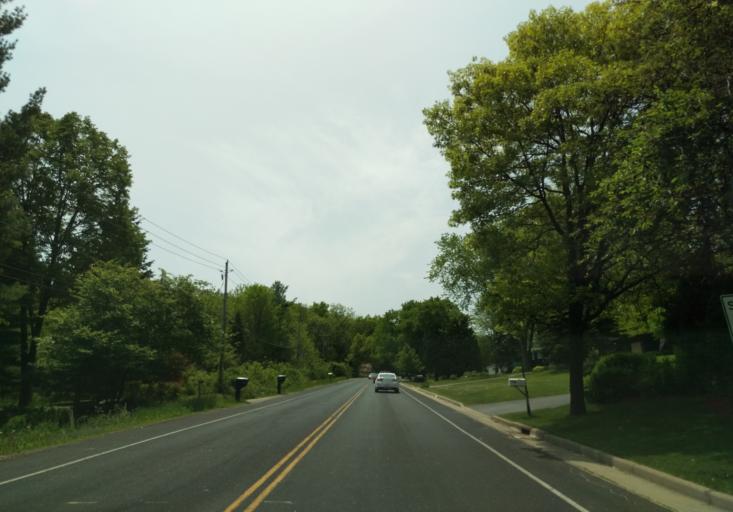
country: US
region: Wisconsin
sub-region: Dane County
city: Cottage Grove
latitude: 43.0810
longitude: -89.2669
